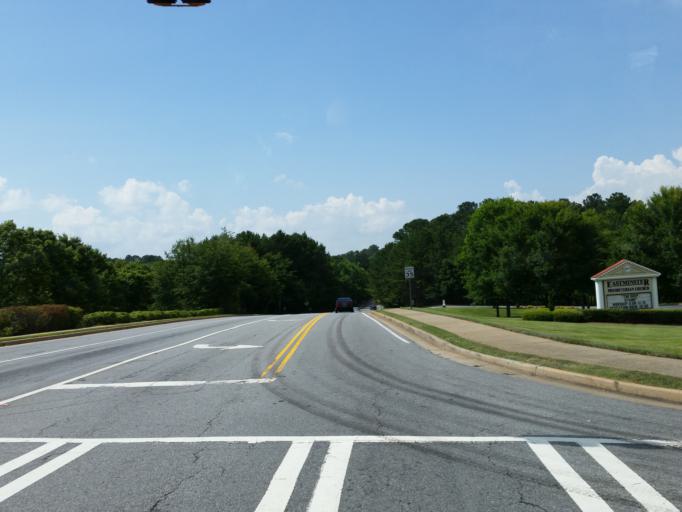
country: US
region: Georgia
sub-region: Cobb County
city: Marietta
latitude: 33.9833
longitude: -84.4625
